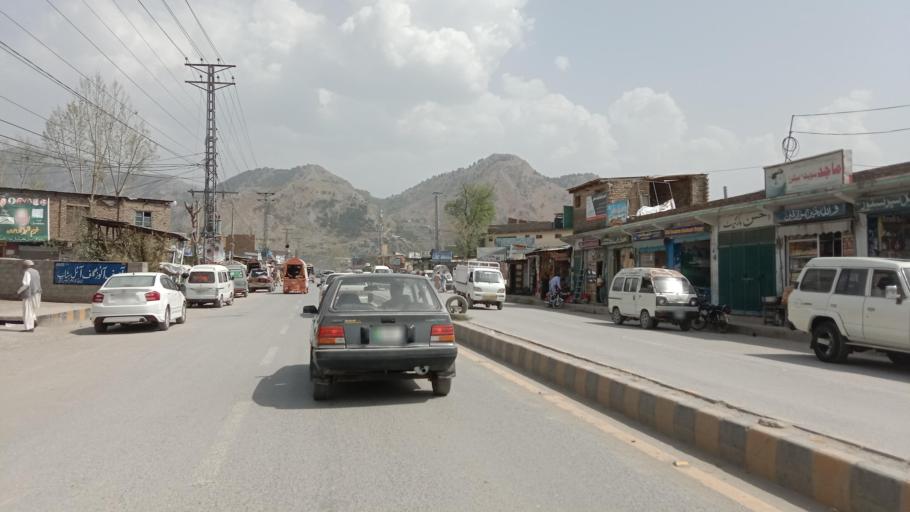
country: PK
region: Khyber Pakhtunkhwa
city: Abbottabad
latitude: 34.1579
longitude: 73.2556
